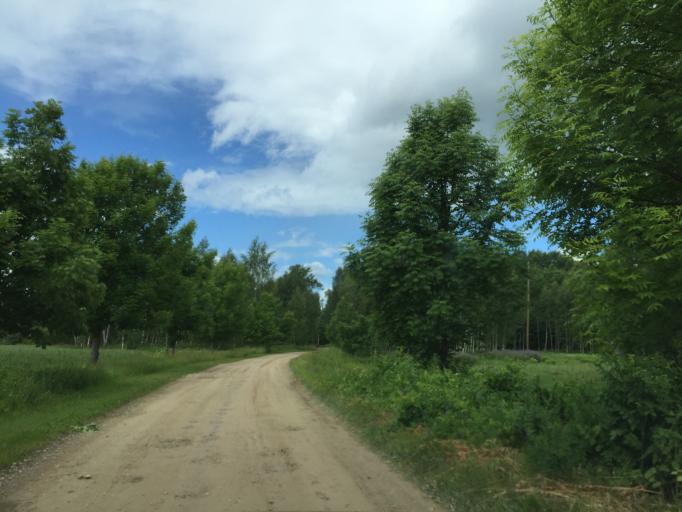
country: LV
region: Lecava
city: Iecava
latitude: 56.5739
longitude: 24.1133
